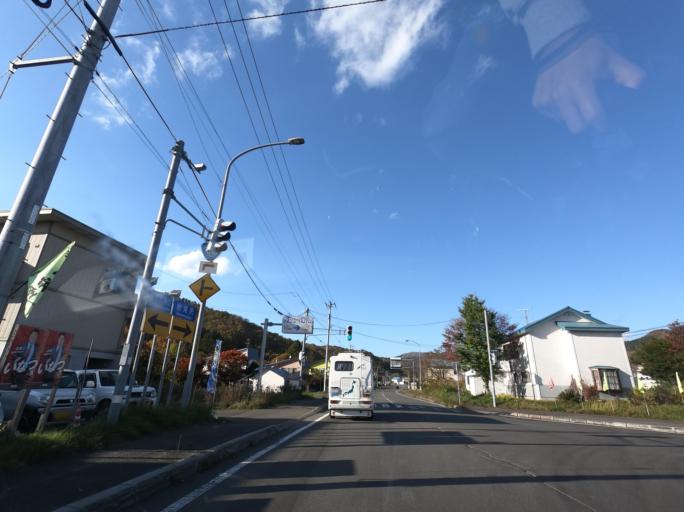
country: JP
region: Hokkaido
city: Iwamizawa
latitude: 42.9954
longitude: 142.0074
